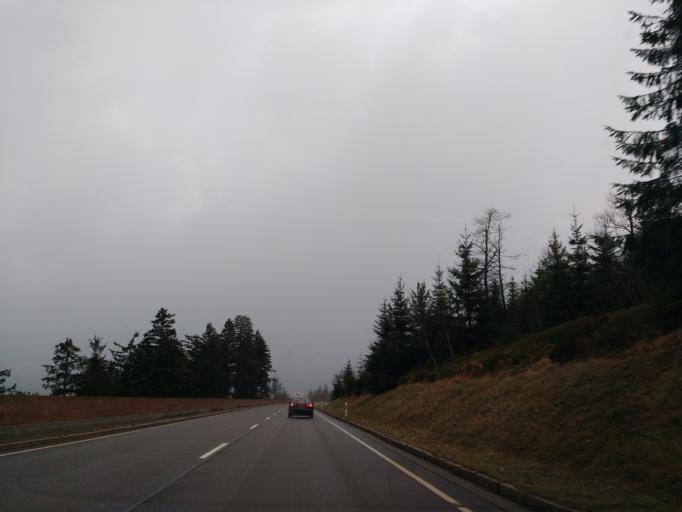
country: DE
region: Baden-Wuerttemberg
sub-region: Freiburg Region
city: Seebach
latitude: 48.5207
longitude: 8.2207
